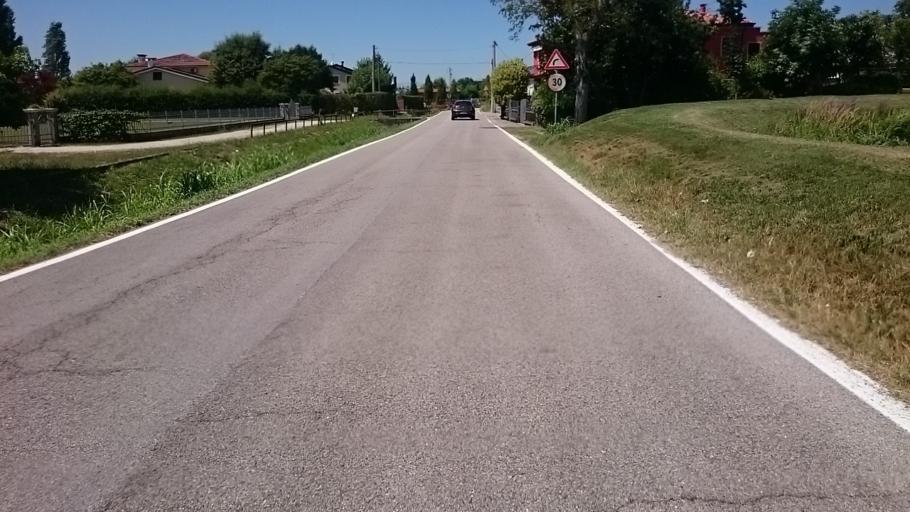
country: IT
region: Veneto
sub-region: Provincia di Padova
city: Campodarsego
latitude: 45.5132
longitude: 11.9292
